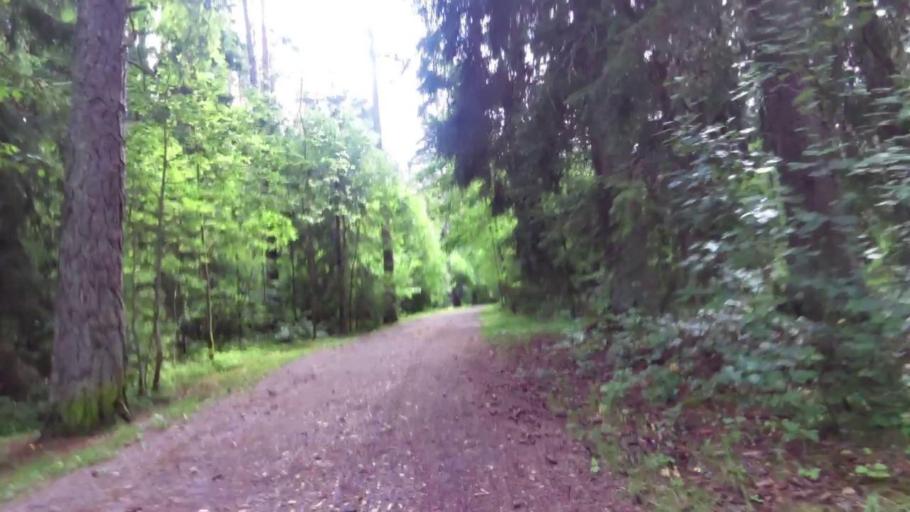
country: SE
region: OEstergoetland
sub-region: Linkopings Kommun
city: Linkoping
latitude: 58.4165
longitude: 15.5762
